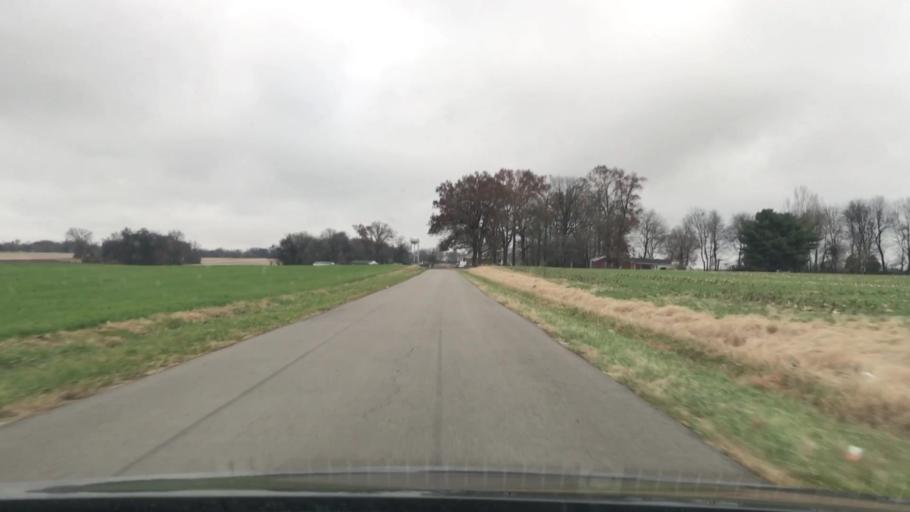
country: US
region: Kentucky
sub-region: Todd County
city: Elkton
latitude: 36.7885
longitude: -87.1512
